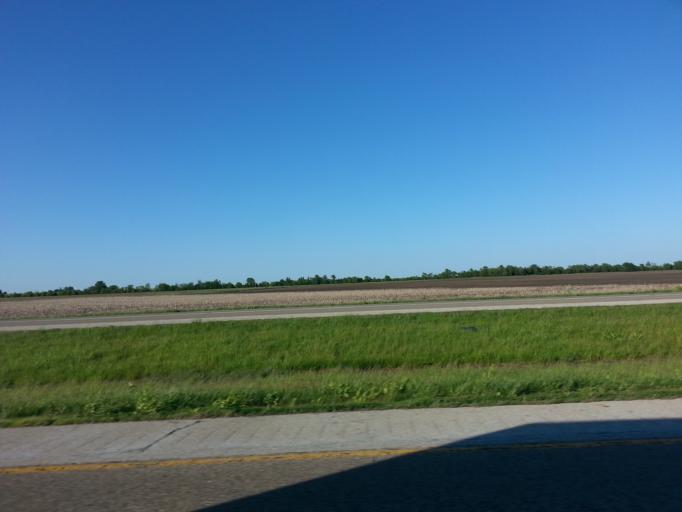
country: US
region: Illinois
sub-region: McLean County
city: Le Roy
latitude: 40.3158
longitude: -88.7324
